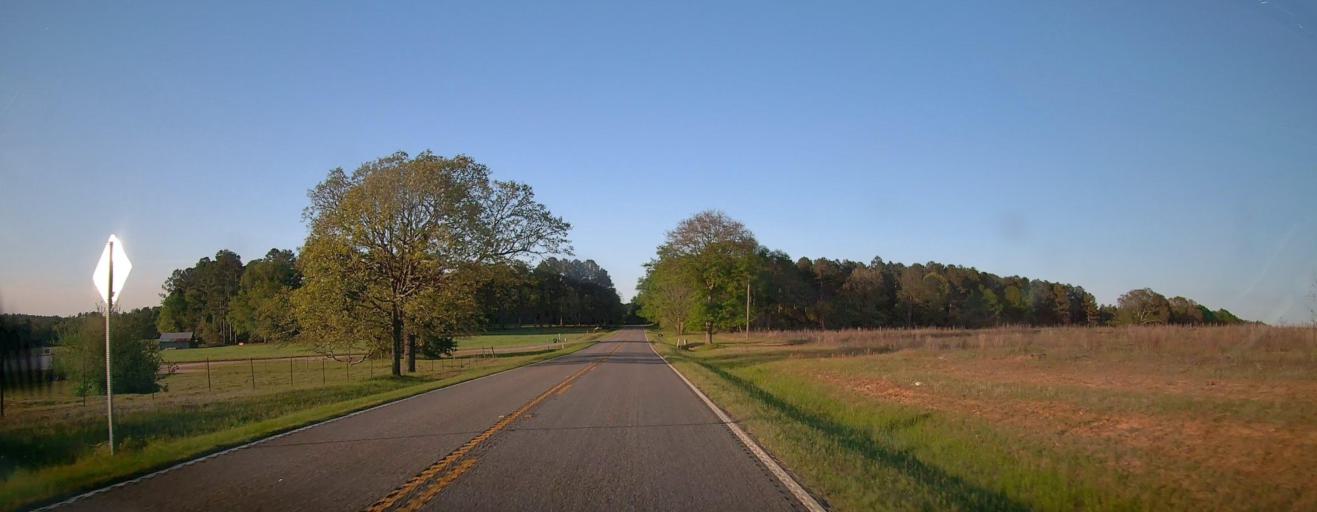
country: US
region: Georgia
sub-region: Marion County
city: Buena Vista
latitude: 32.4016
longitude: -84.4414
